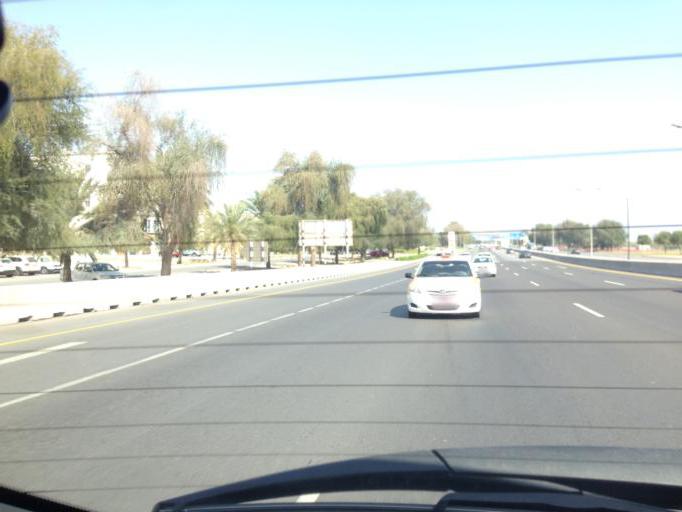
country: OM
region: Muhafazat Masqat
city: As Sib al Jadidah
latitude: 23.5948
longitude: 58.2506
